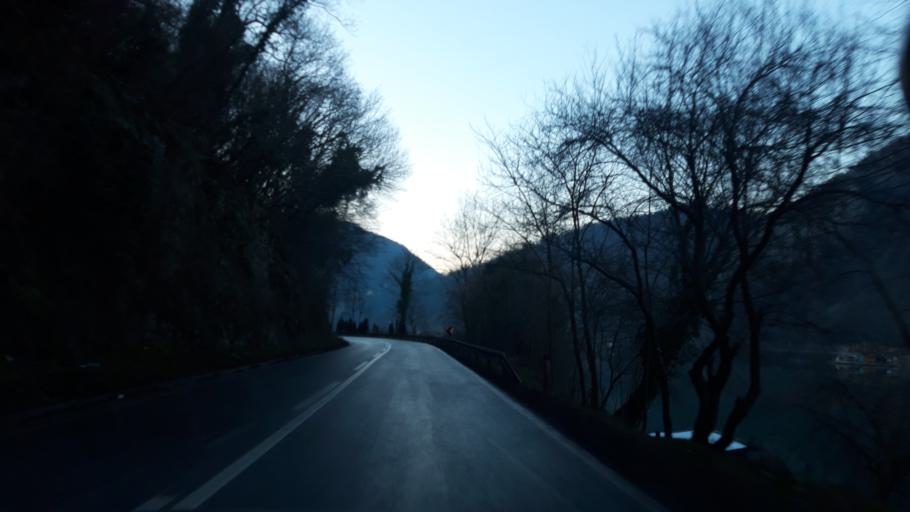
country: RS
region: Central Serbia
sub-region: Macvanski Okrug
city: Mali Zvornik
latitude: 44.3393
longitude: 19.1293
